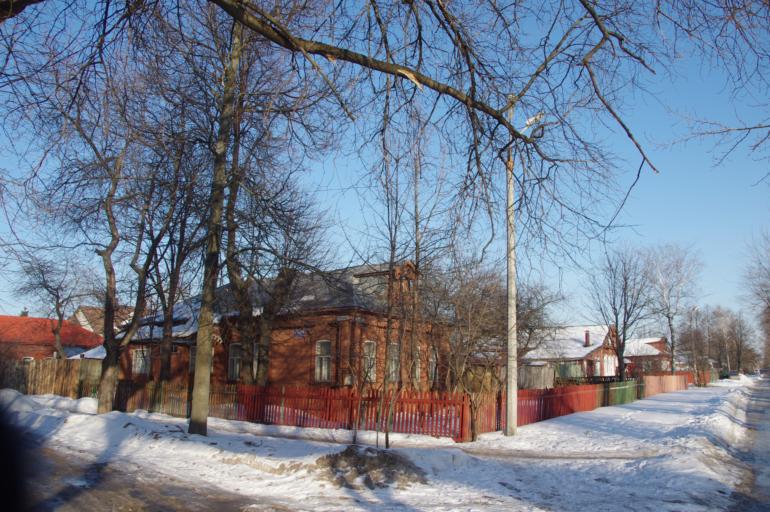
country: RU
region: Moskovskaya
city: Kolomna
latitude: 55.0896
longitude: 38.7848
